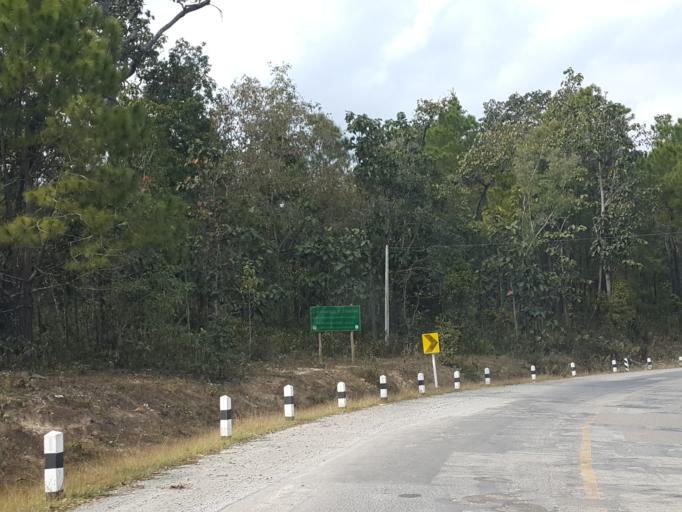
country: TH
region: Chiang Mai
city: Om Koi
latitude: 17.8465
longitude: 98.3709
